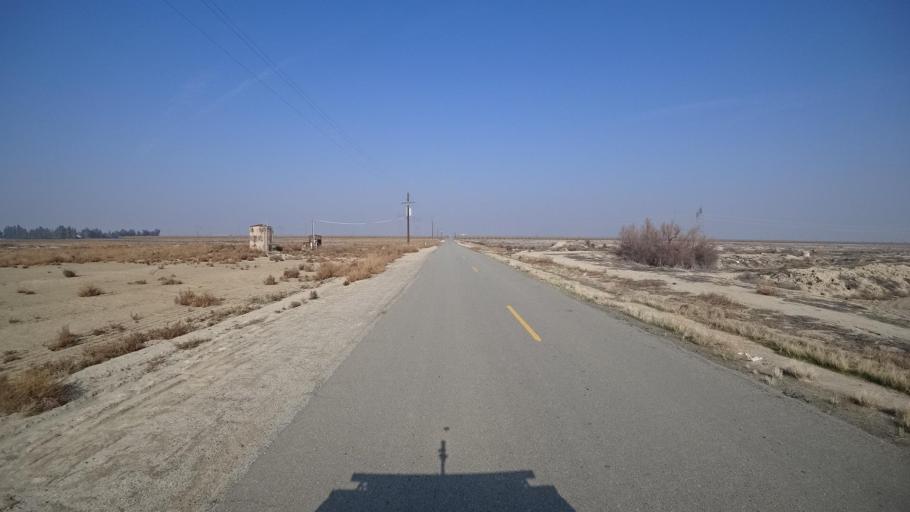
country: US
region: California
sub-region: Kern County
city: Buttonwillow
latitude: 35.3507
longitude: -119.3591
